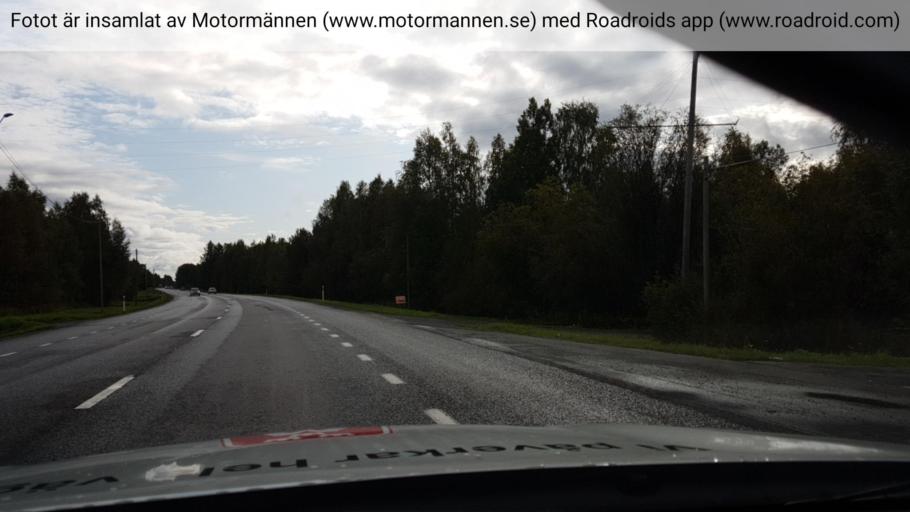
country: SE
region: Norrbotten
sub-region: Bodens Kommun
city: Saevast
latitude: 65.7306
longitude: 21.7778
